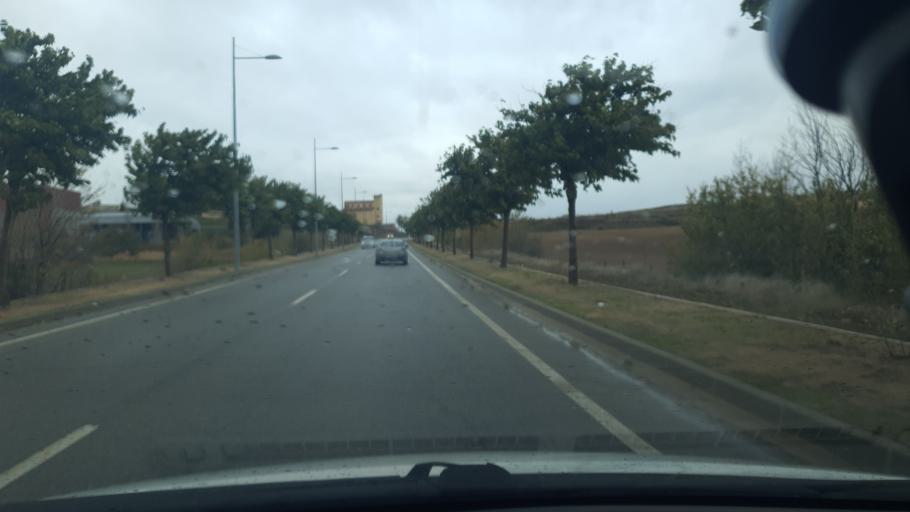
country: ES
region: Castille and Leon
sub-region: Provincia de Segovia
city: Carbonero el Mayor
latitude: 41.1128
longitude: -4.2575
